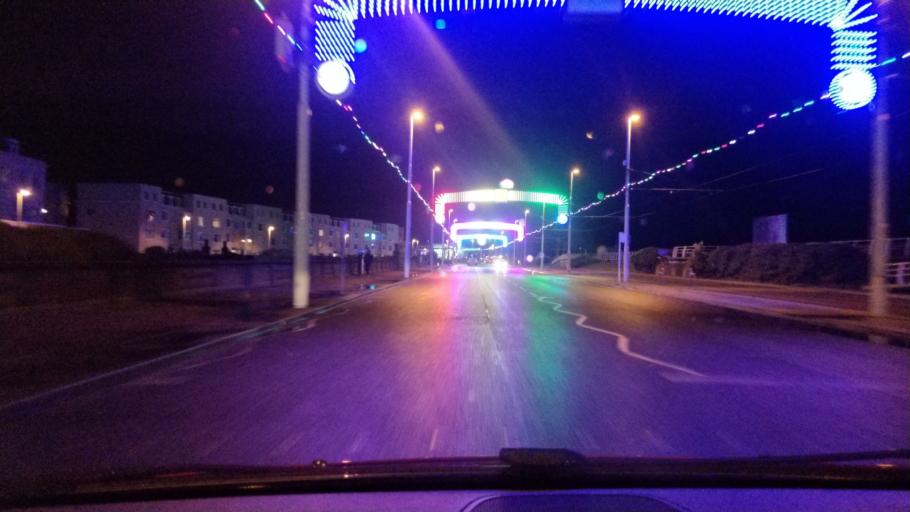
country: GB
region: England
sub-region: Blackpool
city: Blackpool
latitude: 53.7820
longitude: -3.0578
